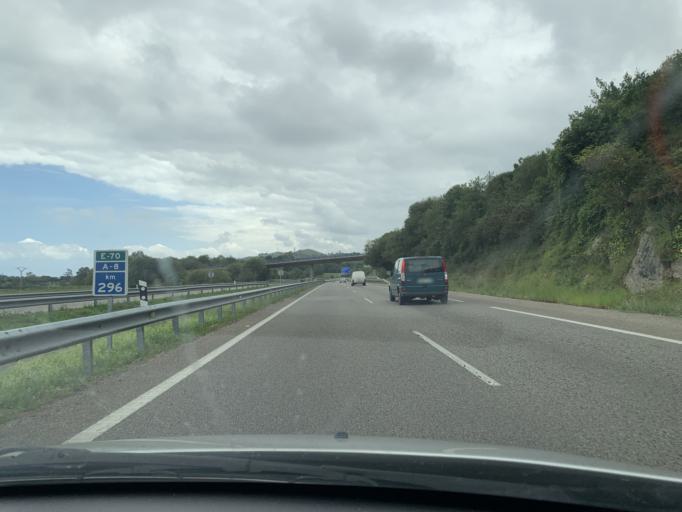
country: ES
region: Asturias
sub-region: Province of Asturias
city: Llanes
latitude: 43.4116
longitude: -4.7798
